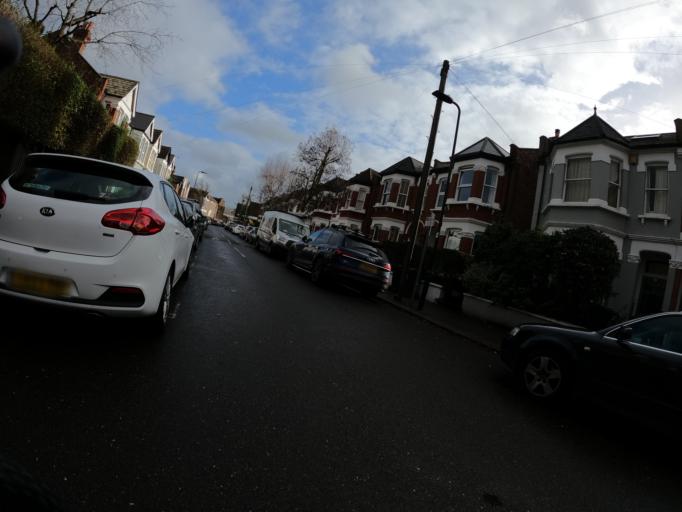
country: GB
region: England
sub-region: Greater London
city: Acton
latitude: 51.5068
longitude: -0.2793
